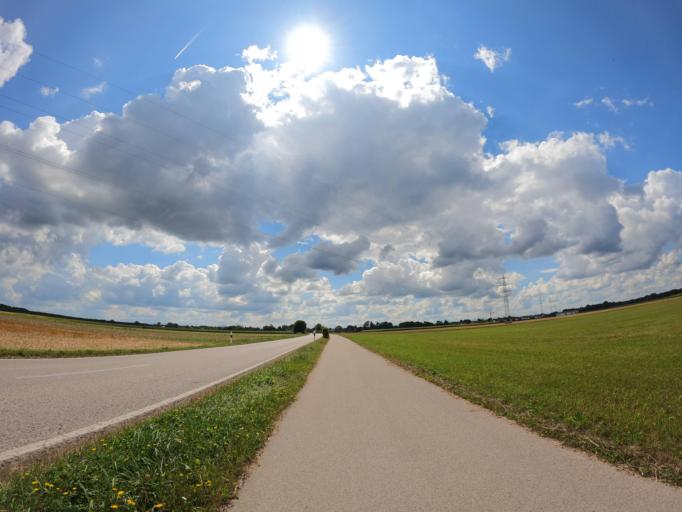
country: DE
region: Bavaria
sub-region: Upper Bavaria
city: Brunnthal
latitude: 48.0143
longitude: 11.6838
